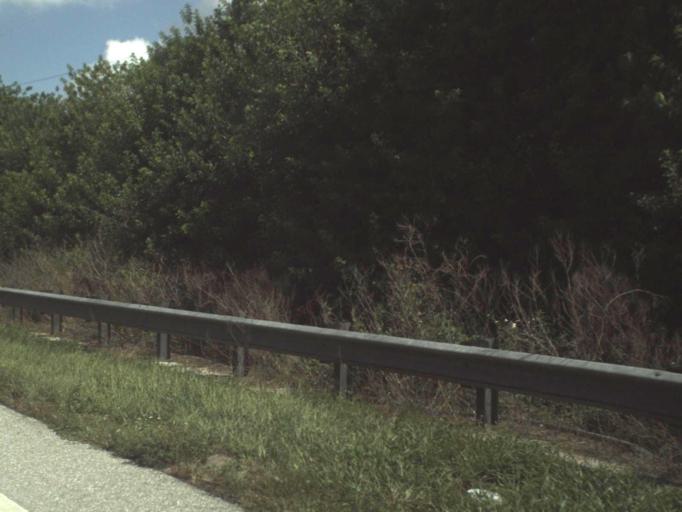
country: US
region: Florida
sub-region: Martin County
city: Indiantown
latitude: 27.1115
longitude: -80.6055
